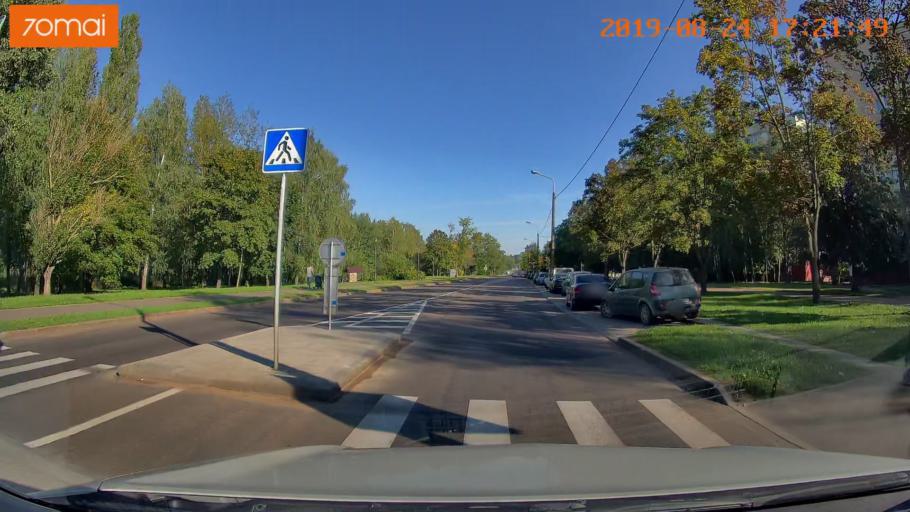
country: BY
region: Minsk
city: Hatava
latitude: 53.8486
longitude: 27.6383
